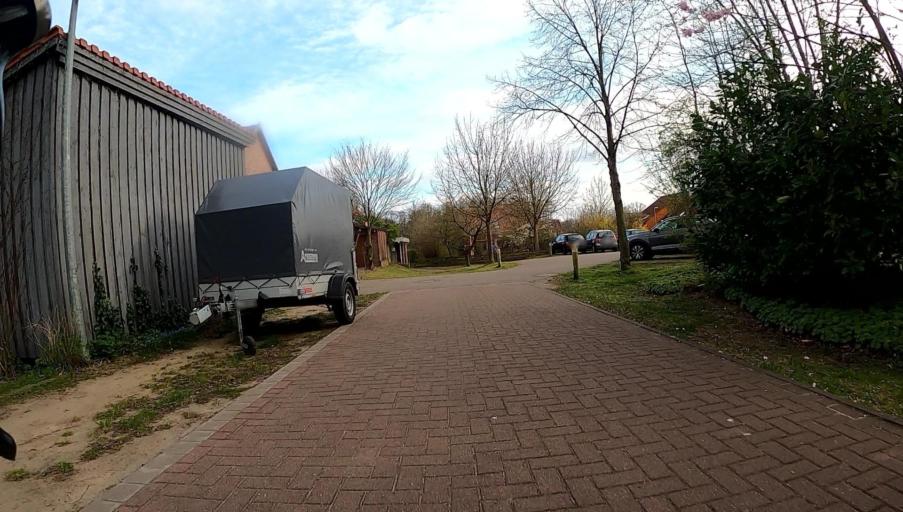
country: DE
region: Lower Saxony
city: Lindwedel
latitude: 52.5568
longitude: 9.6356
